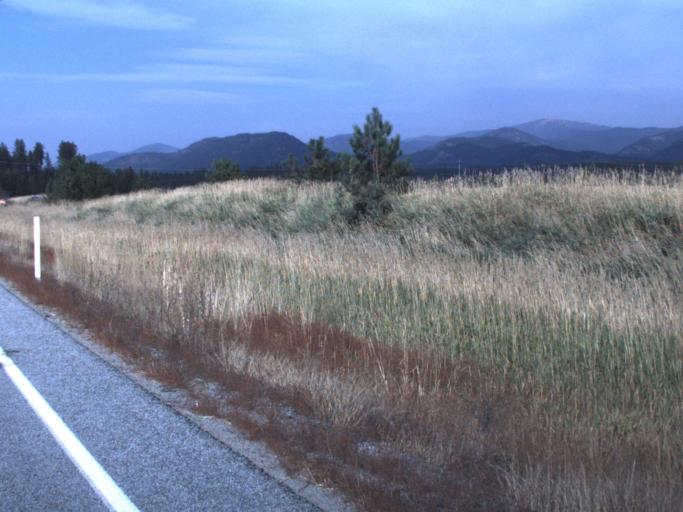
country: US
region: Washington
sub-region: Pend Oreille County
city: Newport
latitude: 48.2904
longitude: -117.2845
